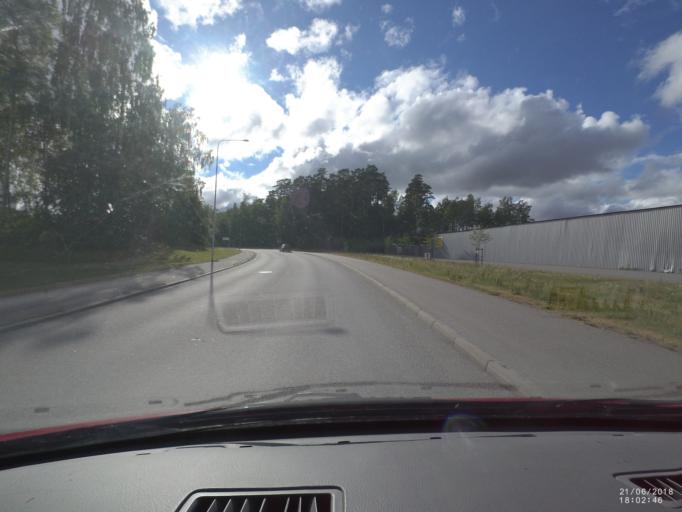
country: SE
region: Soedermanland
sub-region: Nykopings Kommun
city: Nykoping
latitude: 58.7691
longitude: 17.0167
